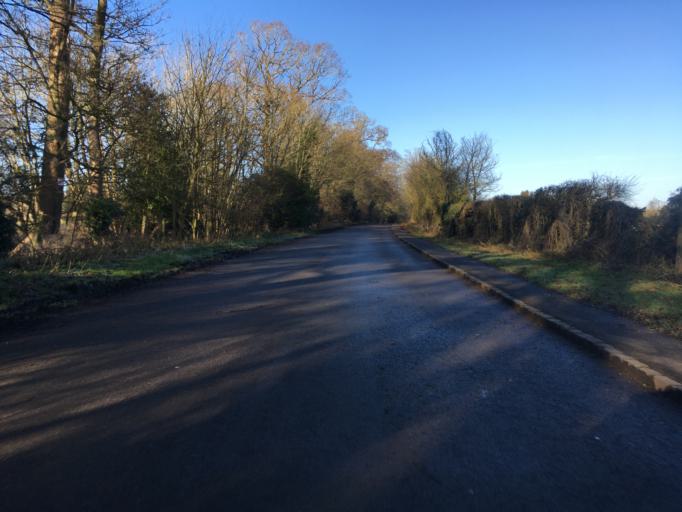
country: GB
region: England
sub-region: Warwickshire
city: Stratford-upon-Avon
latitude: 52.2031
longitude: -1.6547
